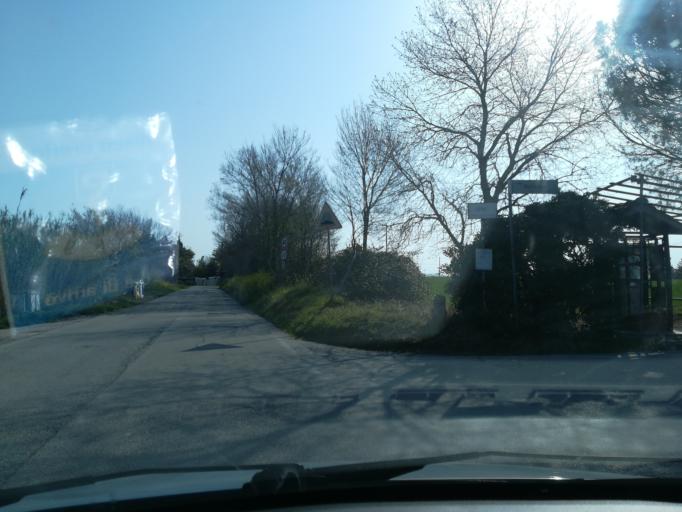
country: IT
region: The Marches
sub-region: Provincia di Macerata
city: Macerata
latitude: 43.3313
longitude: 13.4657
